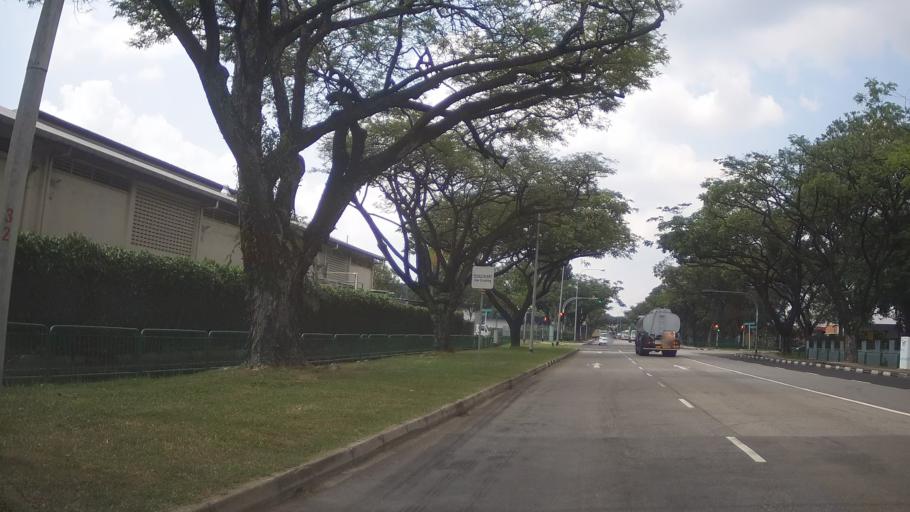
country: MY
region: Johor
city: Johor Bahru
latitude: 1.3191
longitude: 103.6702
